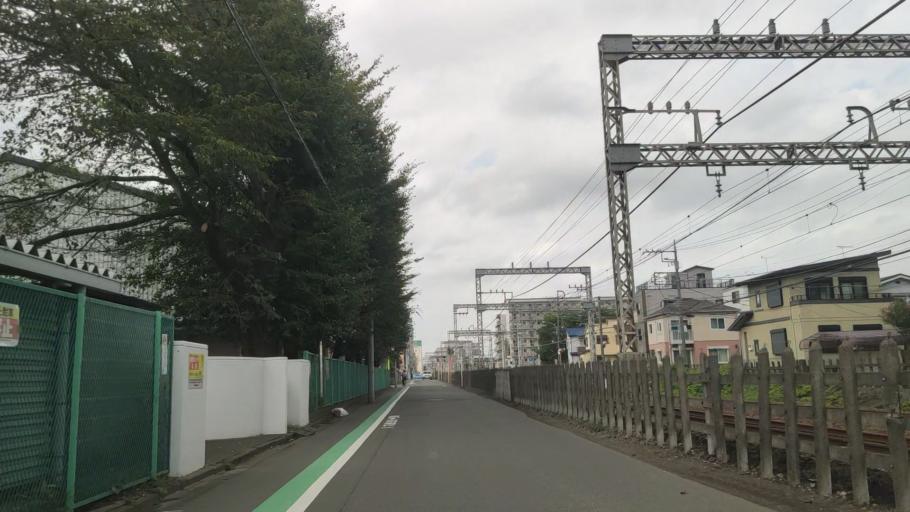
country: JP
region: Kanagawa
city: Minami-rinkan
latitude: 35.4837
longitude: 139.4542
